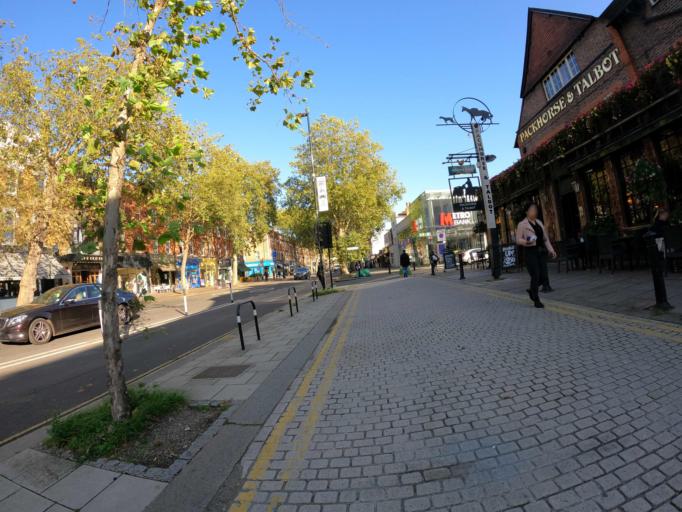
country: GB
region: England
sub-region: Greater London
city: Hammersmith
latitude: 51.4926
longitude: -0.2547
